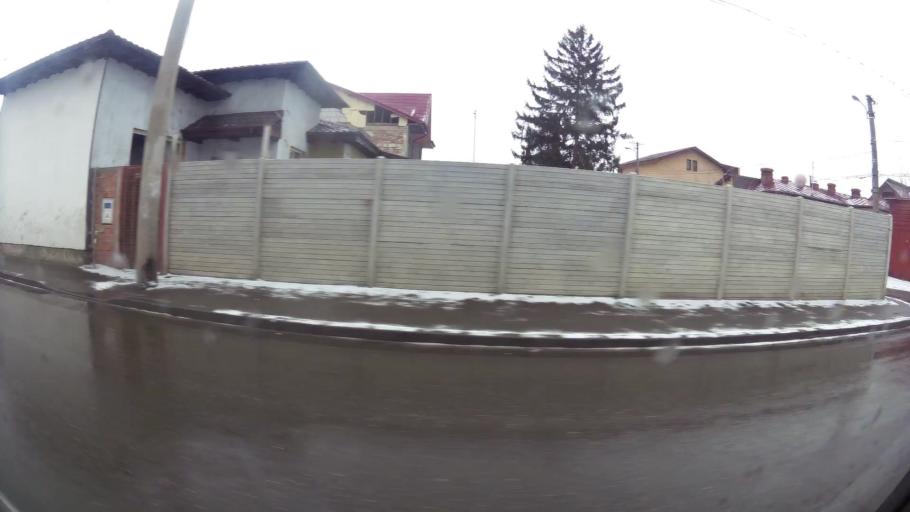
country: RO
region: Prahova
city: Ploiesti
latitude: 44.9498
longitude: 26.0265
